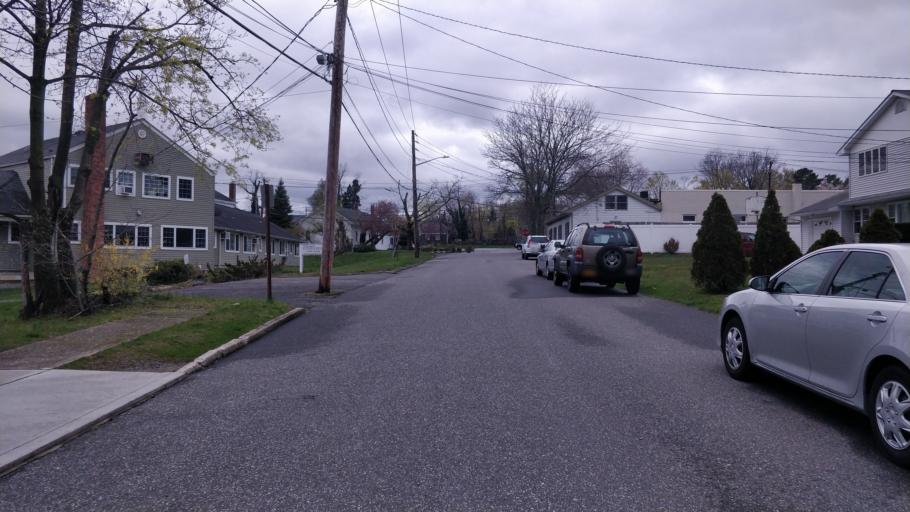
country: US
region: New York
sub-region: Suffolk County
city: East Setauket
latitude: 40.9424
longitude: -73.1056
